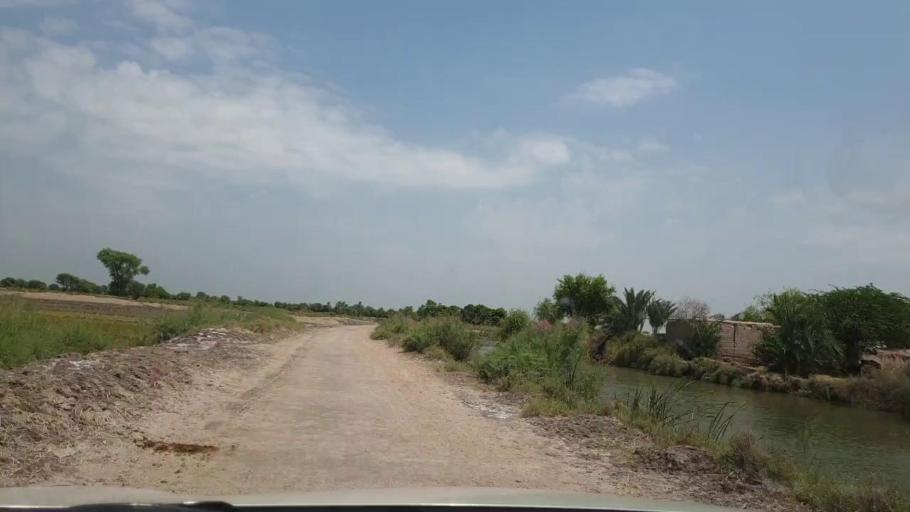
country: PK
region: Sindh
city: Ratodero
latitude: 27.8061
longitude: 68.2268
